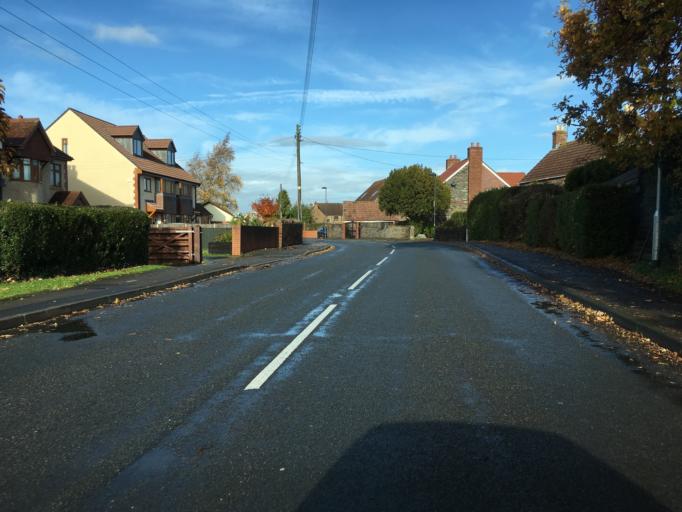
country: GB
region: England
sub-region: South Gloucestershire
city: Yate
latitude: 51.5502
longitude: -2.4352
